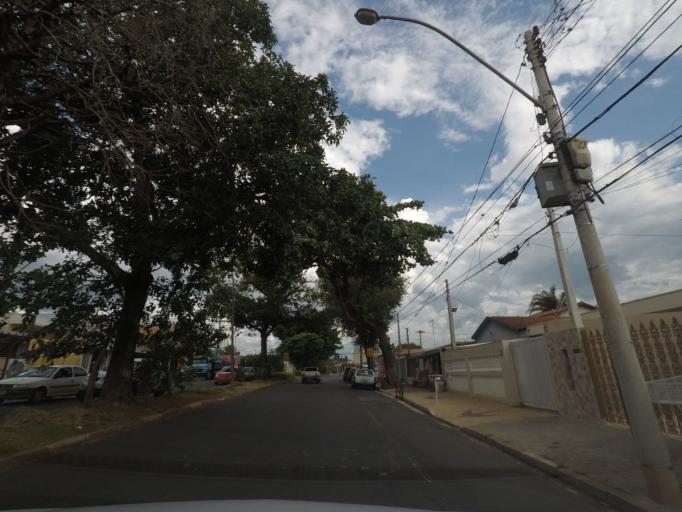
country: BR
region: Sao Paulo
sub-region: Campinas
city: Campinas
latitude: -22.8894
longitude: -47.1075
